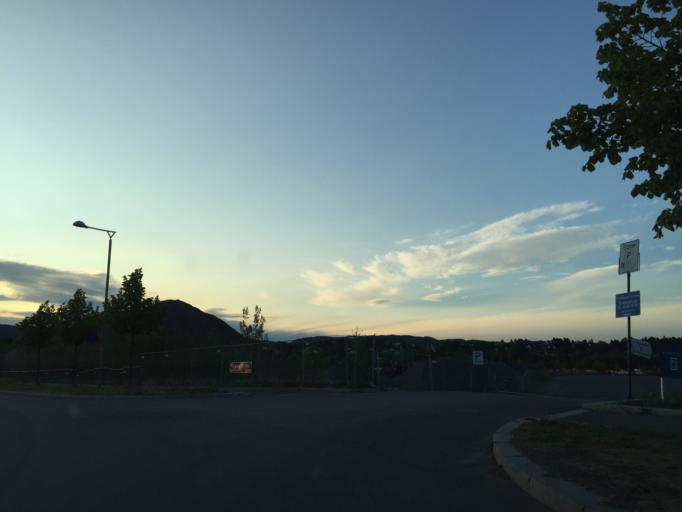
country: NO
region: Akershus
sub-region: Baerum
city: Lysaker
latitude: 59.9000
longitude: 10.6199
